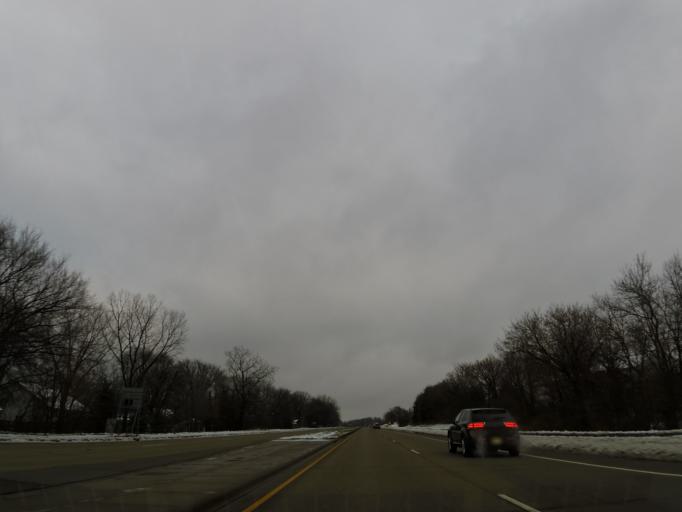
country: US
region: Minnesota
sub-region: Dakota County
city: Burnsville
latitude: 44.7138
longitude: -93.2702
